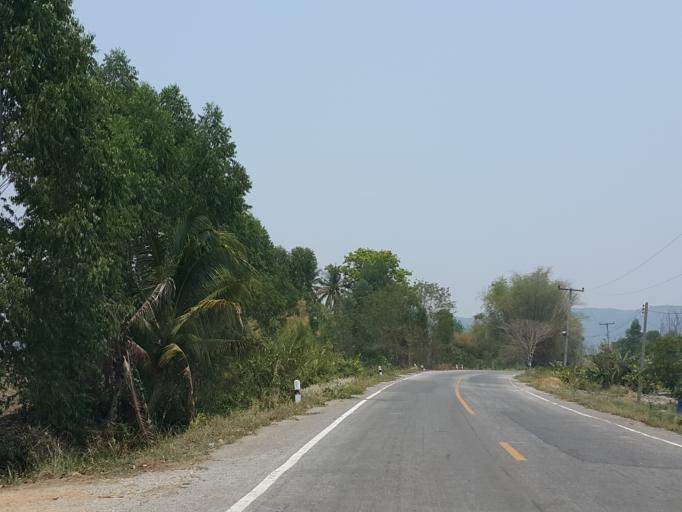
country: TH
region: Kamphaeng Phet
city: Pang Sila Thong
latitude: 16.0556
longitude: 99.3637
